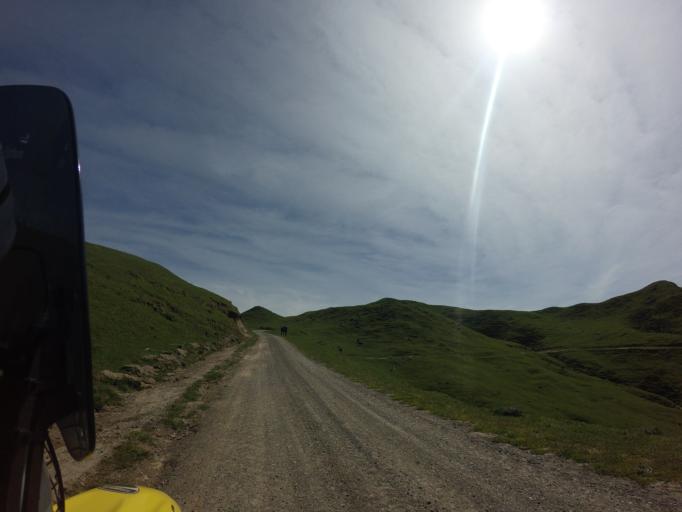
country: NZ
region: Bay of Plenty
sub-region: Opotiki District
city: Opotiki
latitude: -38.4528
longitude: 177.3659
